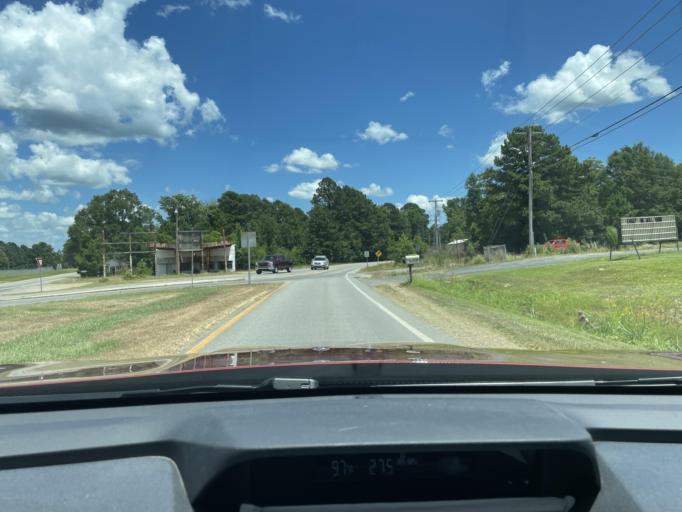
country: US
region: Arkansas
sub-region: Drew County
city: Monticello
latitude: 33.6289
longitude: -91.7585
